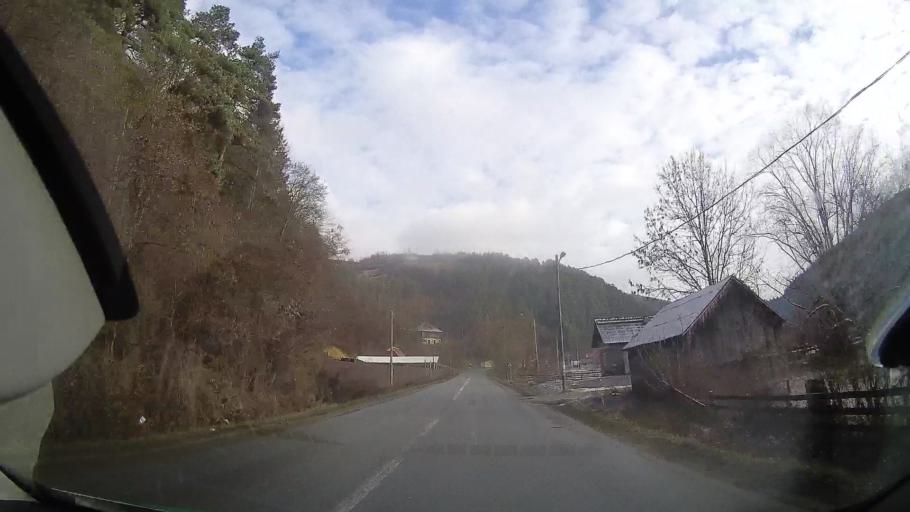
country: RO
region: Alba
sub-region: Comuna Bistra
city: Bistra
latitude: 46.3817
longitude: 23.1236
